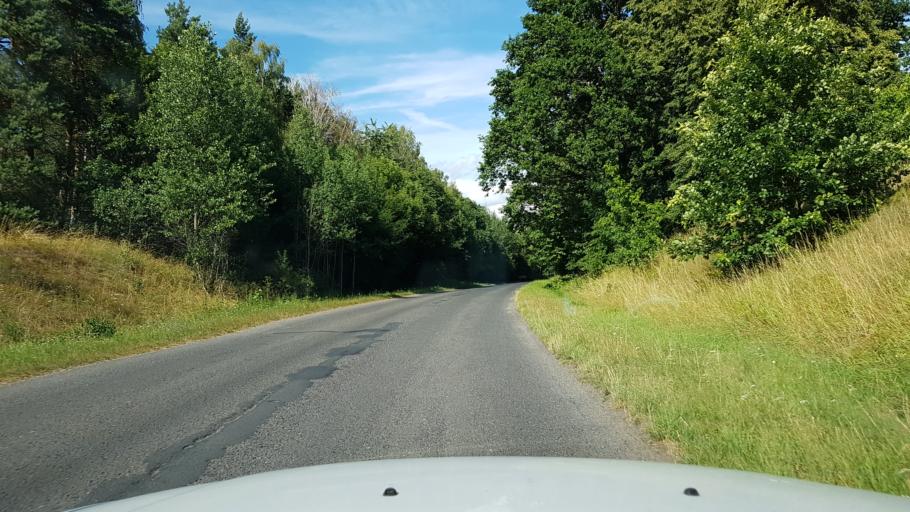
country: PL
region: West Pomeranian Voivodeship
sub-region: Powiat gryfinski
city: Stare Czarnowo
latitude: 53.2951
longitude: 14.7872
